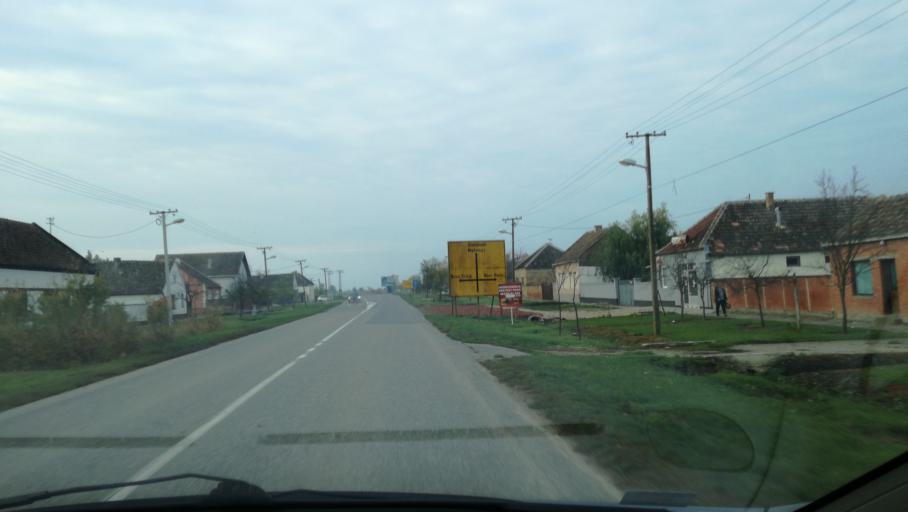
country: RS
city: Basaid
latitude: 45.6369
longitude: 20.4110
